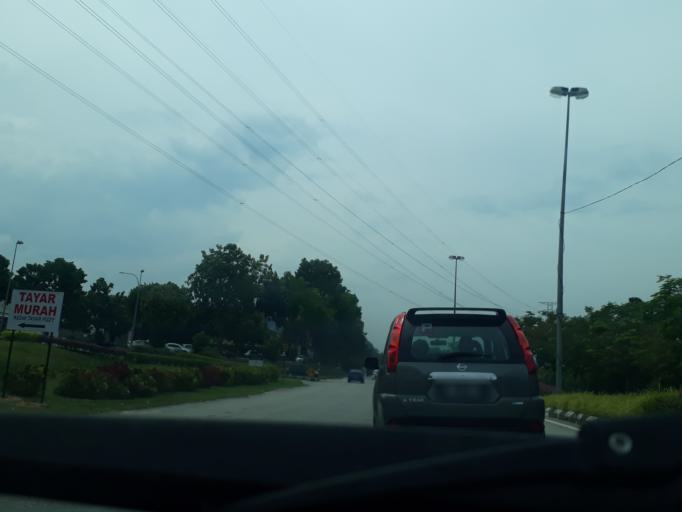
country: MY
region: Perak
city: Ipoh
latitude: 4.6299
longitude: 101.1536
